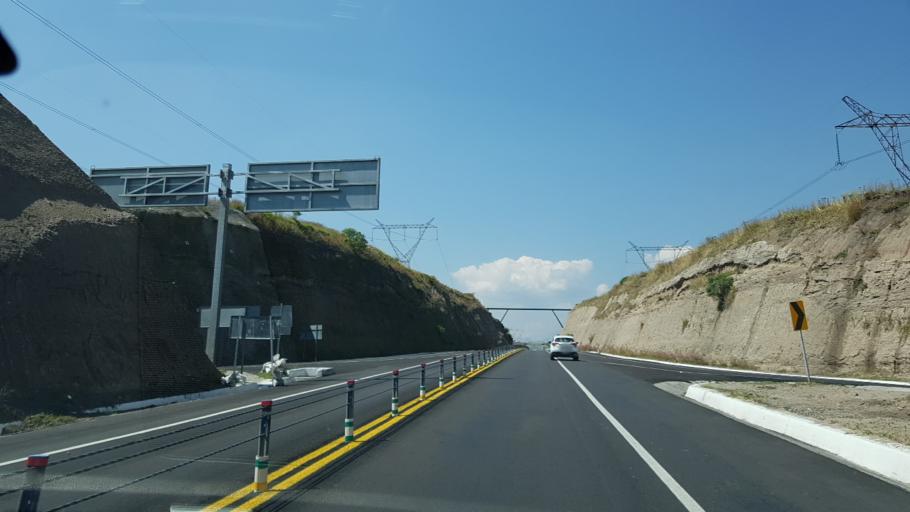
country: MX
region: Mexico
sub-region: Almoloya de Juarez
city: El Plan
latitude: 19.3810
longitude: -99.8093
